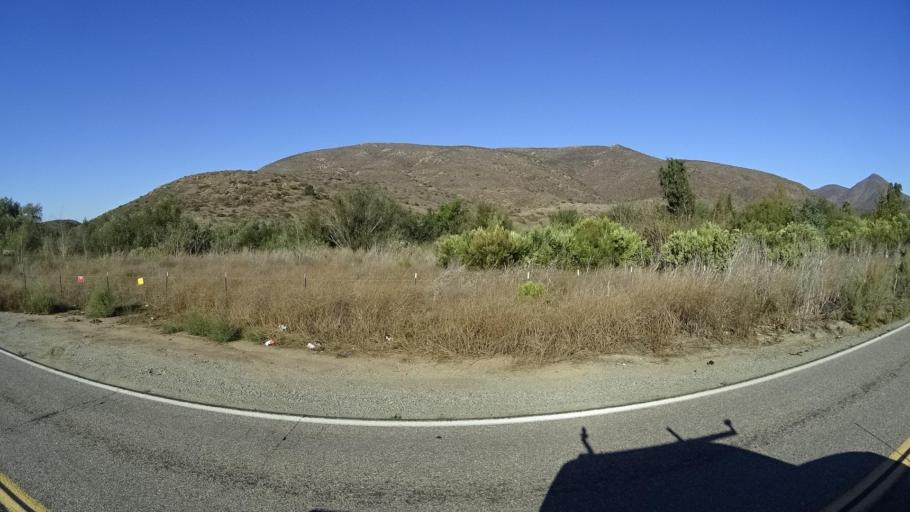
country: US
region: California
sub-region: San Diego County
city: Jamul
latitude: 32.6467
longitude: -116.8694
